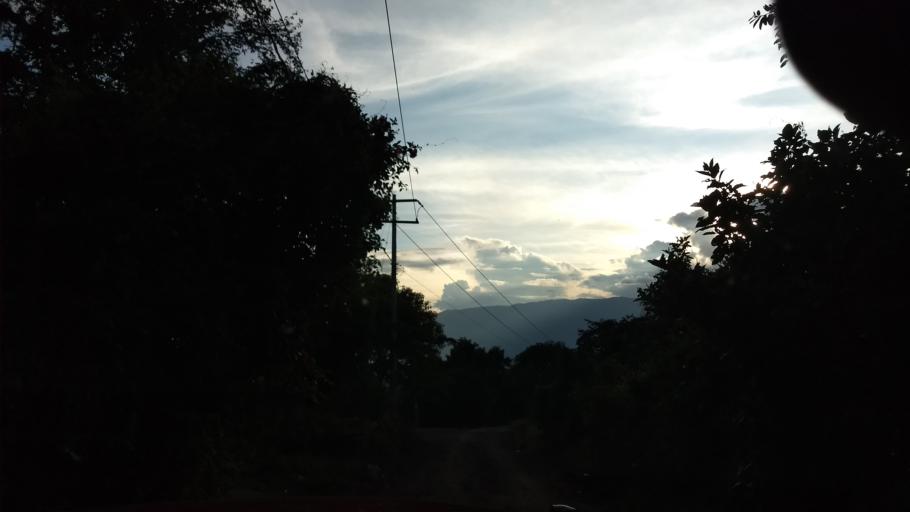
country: MX
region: Jalisco
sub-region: San Gabriel
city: Alista
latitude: 19.5077
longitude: -103.7528
